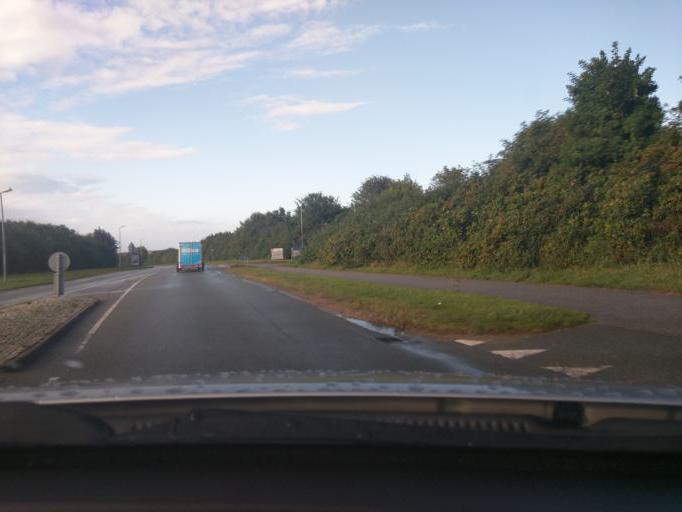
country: DK
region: Central Jutland
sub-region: Viborg Kommune
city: Viborg
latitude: 56.4633
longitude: 9.3773
